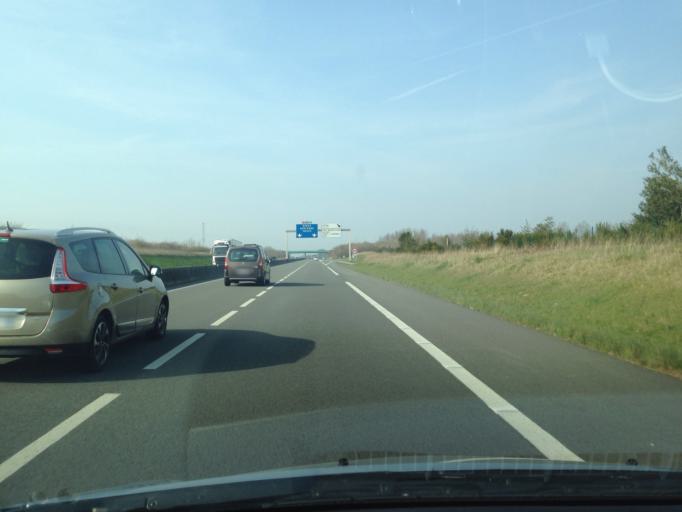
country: FR
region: Picardie
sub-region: Departement de la Somme
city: Nouvion
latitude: 50.2469
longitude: 1.7505
